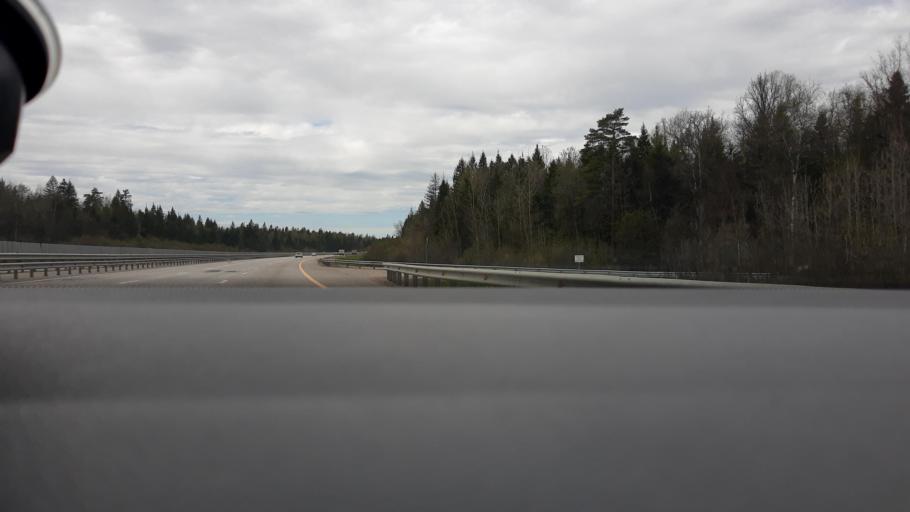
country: RU
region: Moskovskaya
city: Yershovo
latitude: 55.8306
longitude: 36.8621
